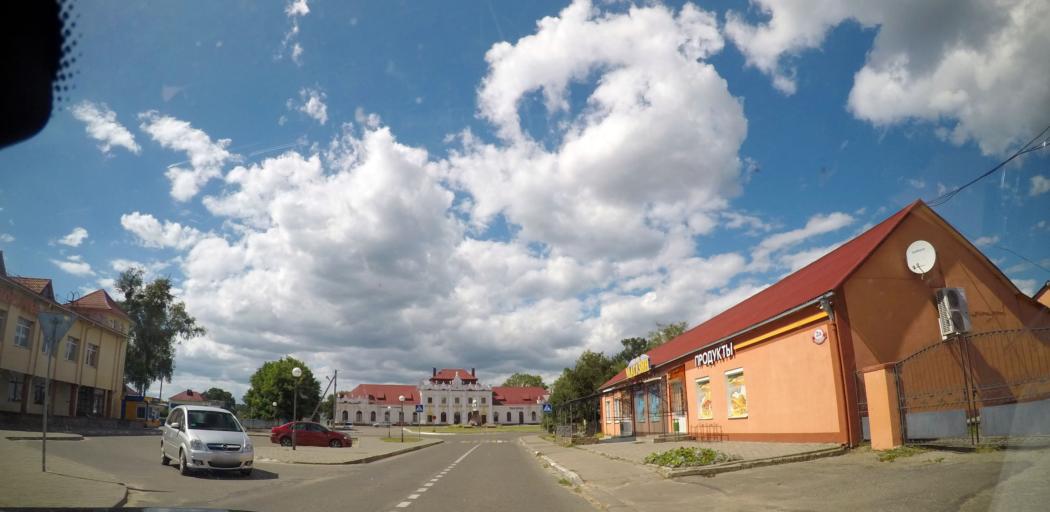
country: LT
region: Alytaus apskritis
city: Druskininkai
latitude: 53.8850
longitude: 24.1360
